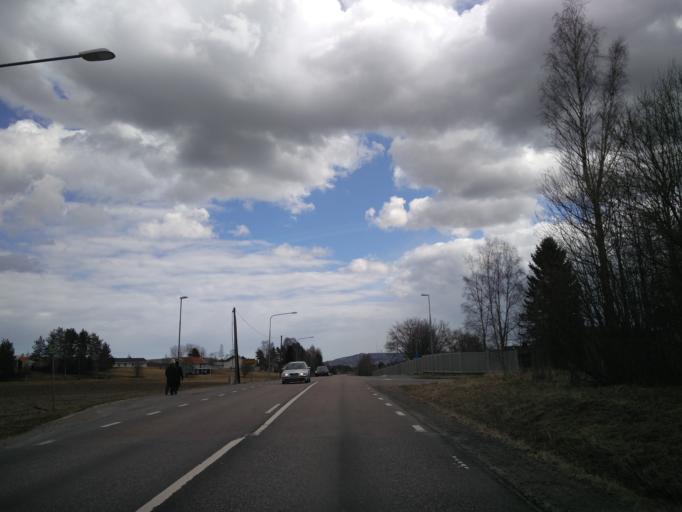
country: SE
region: Vaesternorrland
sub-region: Sundsvalls Kommun
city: Sundsvall
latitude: 62.4157
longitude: 17.2136
